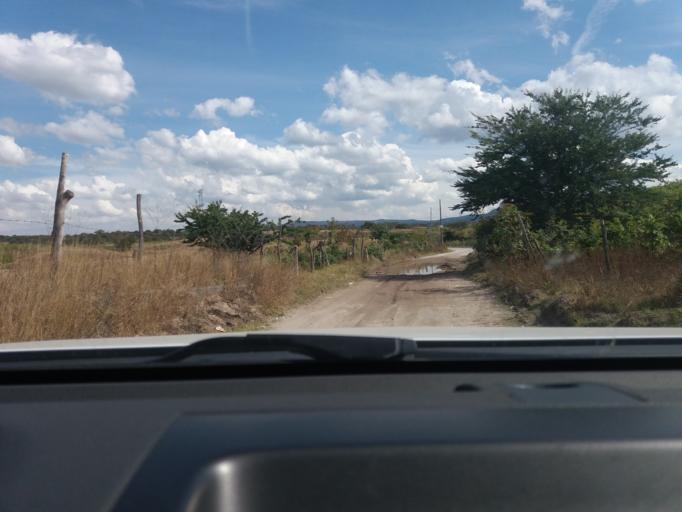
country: MX
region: Jalisco
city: Tala
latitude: 20.6573
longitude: -103.6915
